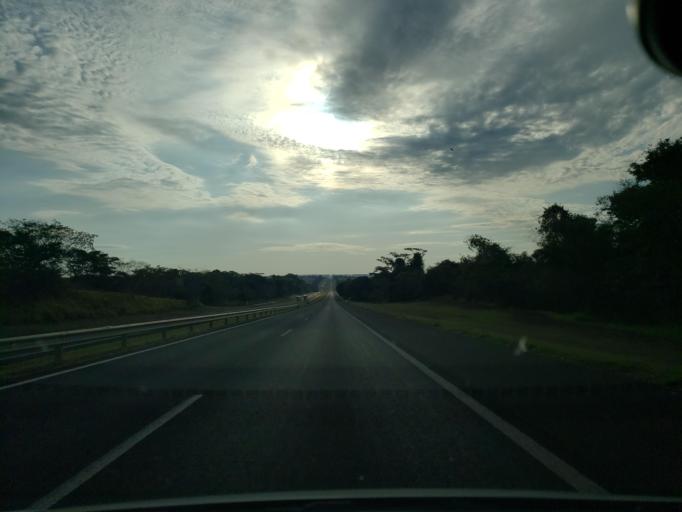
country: BR
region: Sao Paulo
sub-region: Mirandopolis
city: Mirandopolis
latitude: -21.1051
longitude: -51.0327
